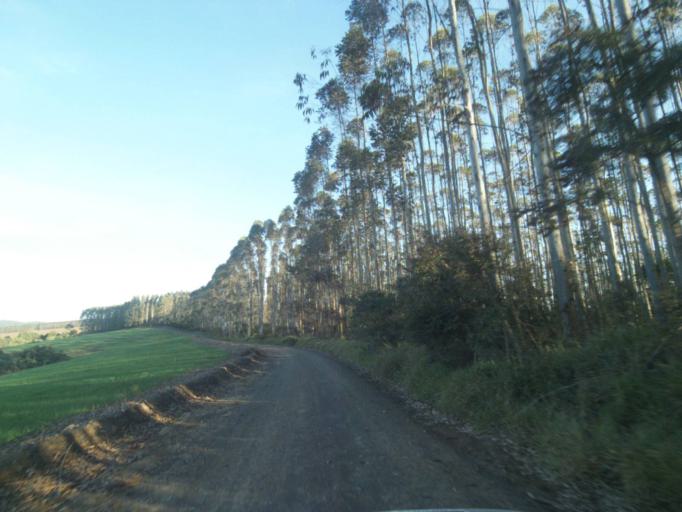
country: BR
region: Parana
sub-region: Telemaco Borba
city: Telemaco Borba
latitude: -24.4362
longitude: -50.6025
